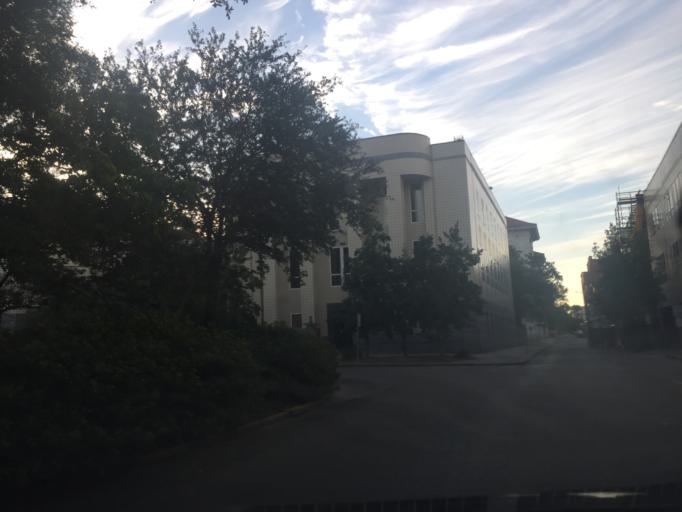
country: US
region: Georgia
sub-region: Chatham County
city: Savannah
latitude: 32.0782
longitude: -81.0946
